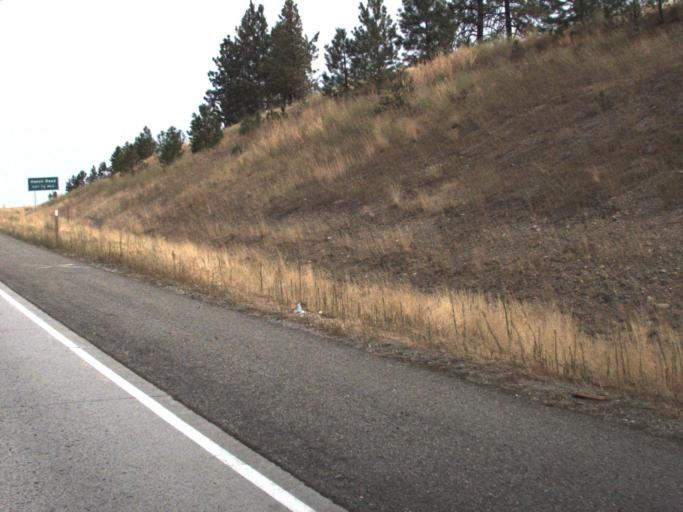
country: US
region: Washington
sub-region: Spokane County
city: Fairwood
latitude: 47.7925
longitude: -117.4084
